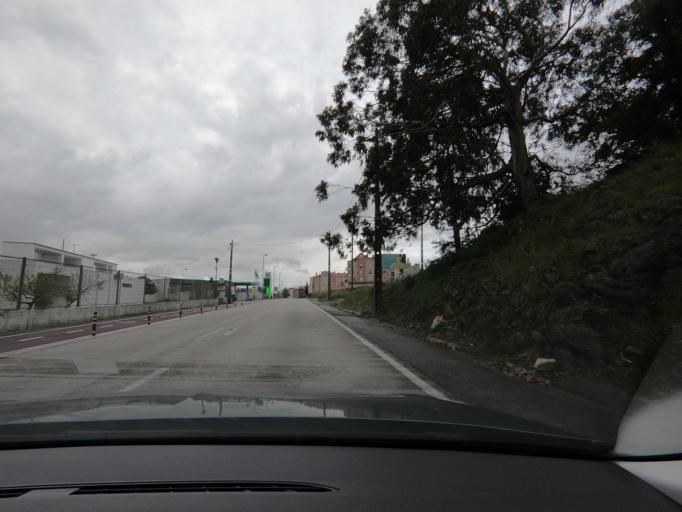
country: PT
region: Lisbon
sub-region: Sintra
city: Sintra
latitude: 38.8001
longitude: -9.3576
